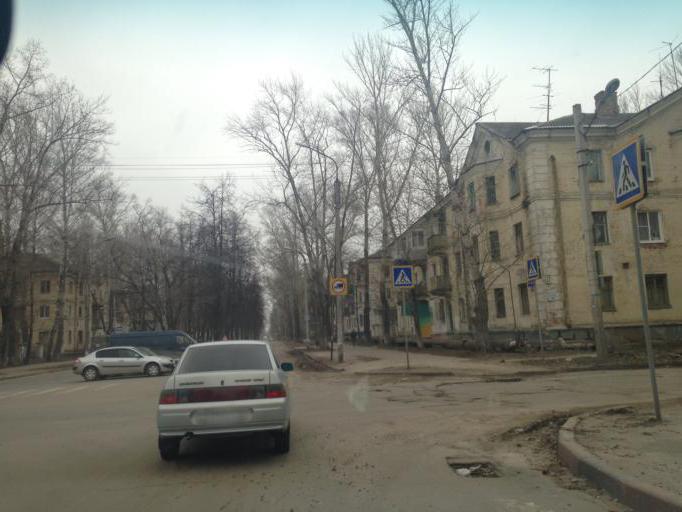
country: RU
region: Ulyanovsk
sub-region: Ulyanovskiy Rayon
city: Ulyanovsk
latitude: 54.2941
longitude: 48.2978
